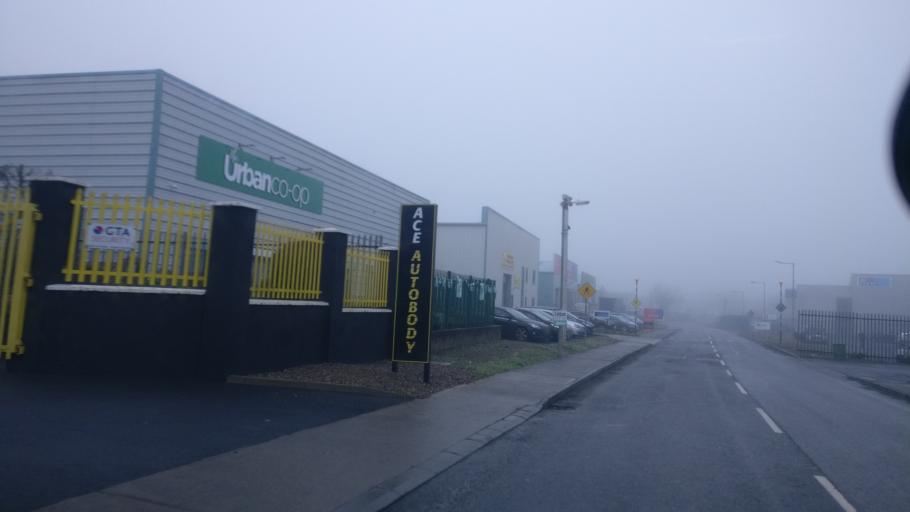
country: IE
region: Munster
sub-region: County Limerick
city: Luimneach
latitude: 52.6484
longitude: -8.5895
